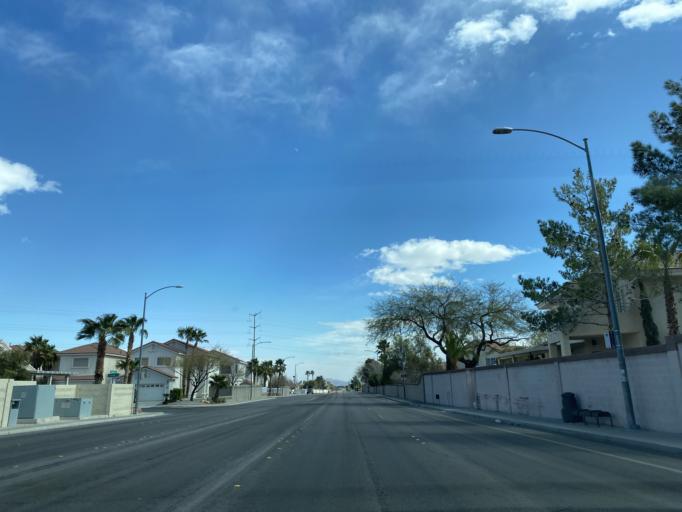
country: US
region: Nevada
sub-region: Clark County
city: Spring Valley
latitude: 36.2260
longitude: -115.2728
